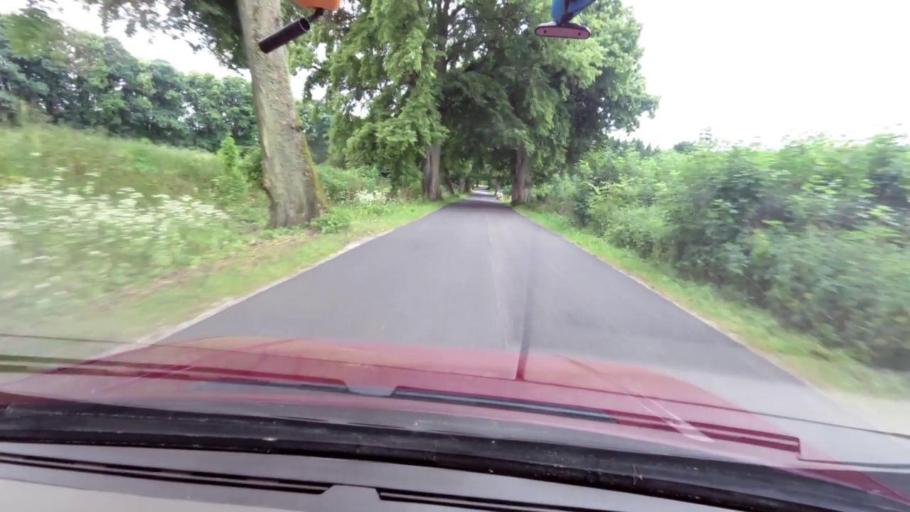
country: PL
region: Pomeranian Voivodeship
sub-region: Powiat slupski
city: Kepice
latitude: 54.2143
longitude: 16.8351
